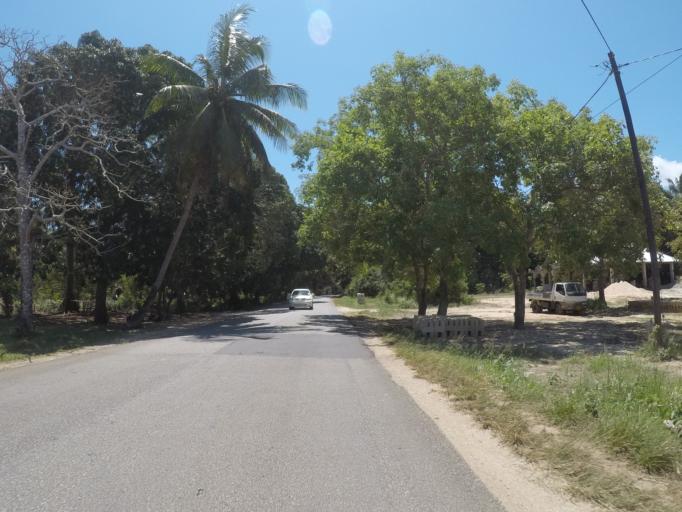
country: TZ
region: Zanzibar Central/South
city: Koani
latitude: -6.2325
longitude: 39.3250
